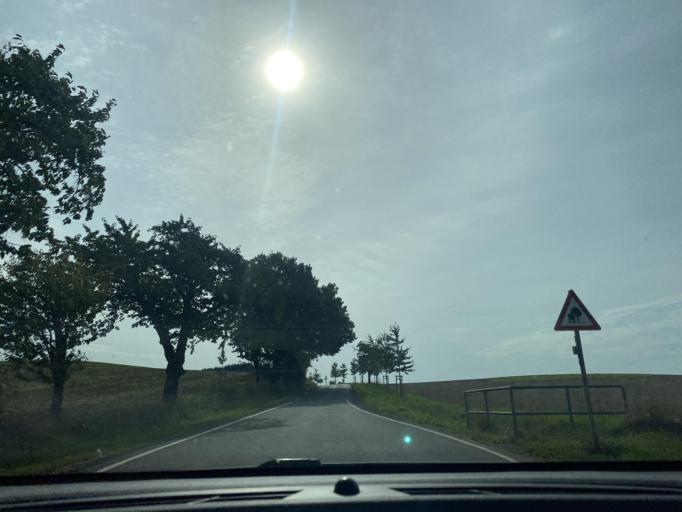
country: DE
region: Saxony
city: Quitzdorf
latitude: 51.2421
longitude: 14.7700
